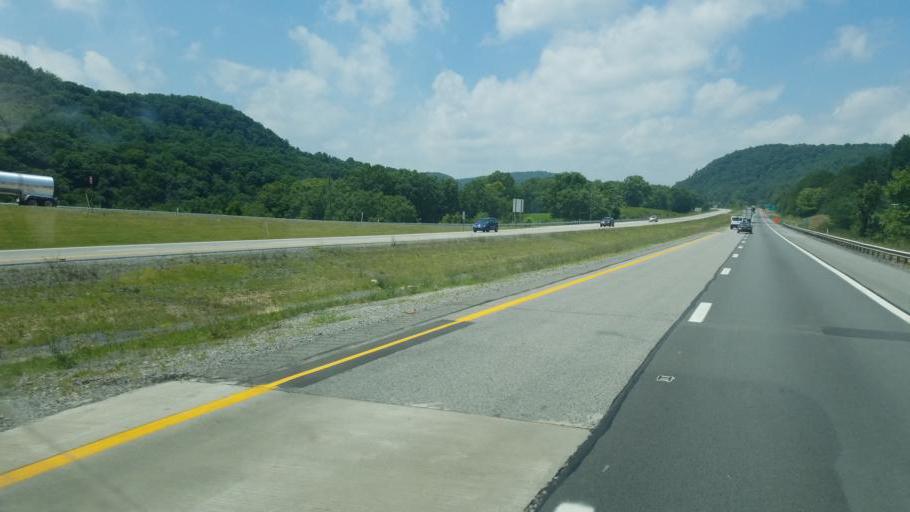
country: US
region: West Virginia
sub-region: Mercer County
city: Athens
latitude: 37.4878
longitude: -81.0815
